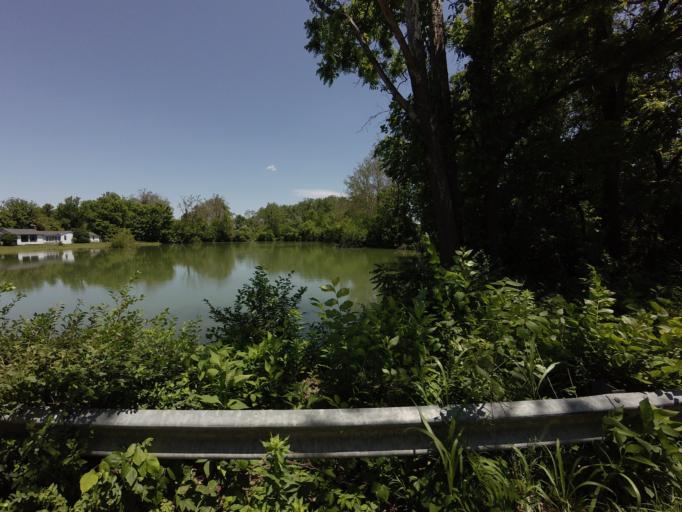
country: US
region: West Virginia
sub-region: Jefferson County
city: Ranson
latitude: 39.3136
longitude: -77.8198
